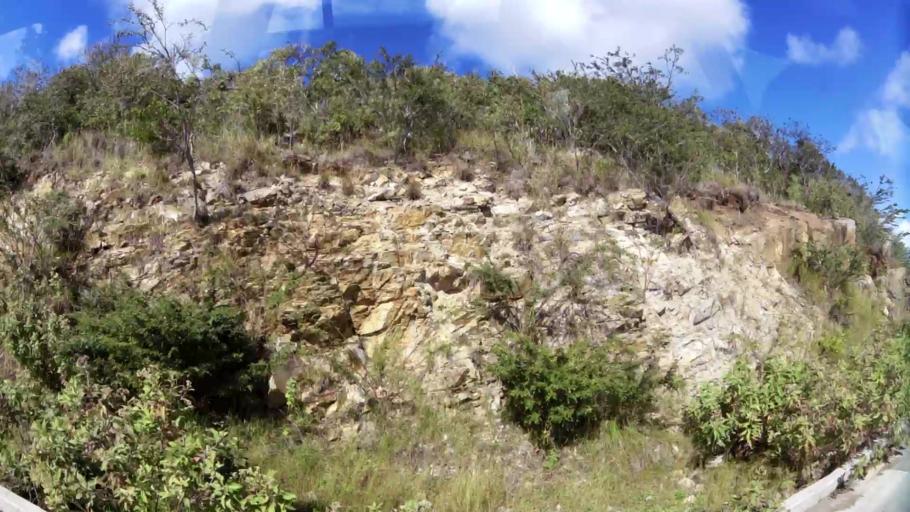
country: VG
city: Tortola
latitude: 18.4930
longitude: -64.3999
